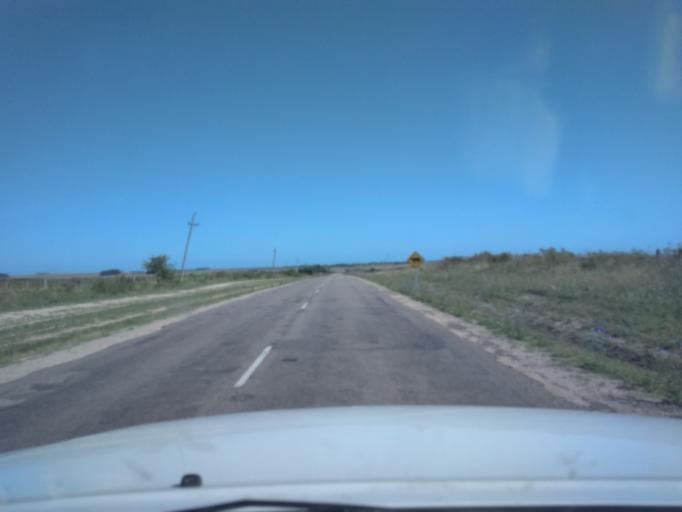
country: UY
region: Canelones
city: San Ramon
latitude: -34.2341
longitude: -55.9276
